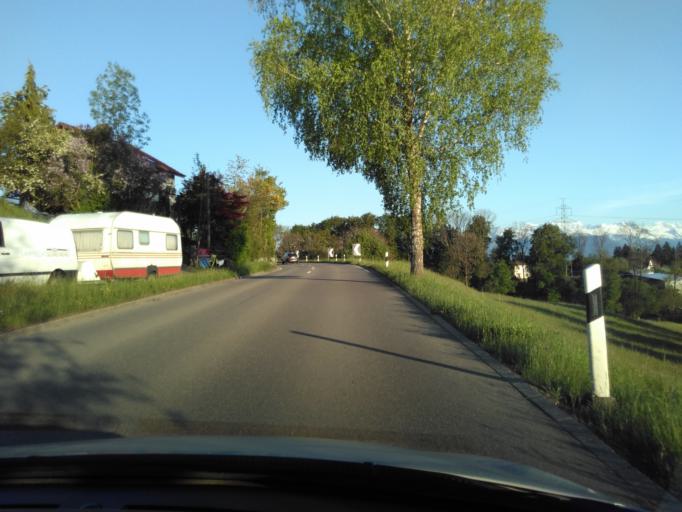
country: CH
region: Zurich
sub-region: Bezirk Hinwil
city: Hadlikon
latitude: 47.2767
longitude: 8.8627
